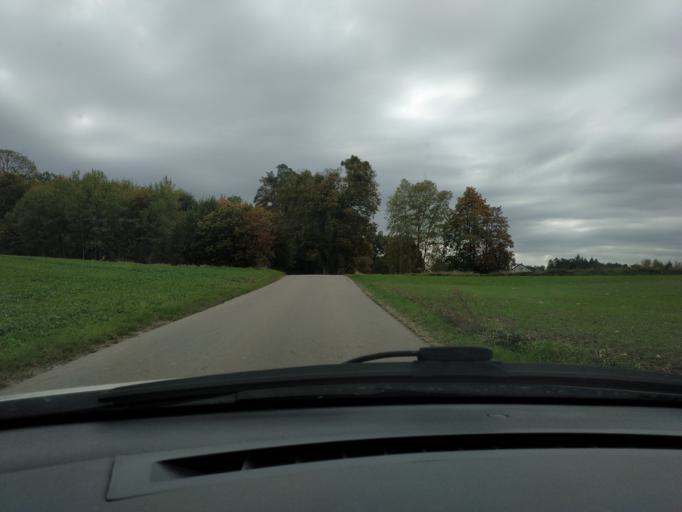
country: PL
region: Warmian-Masurian Voivodeship
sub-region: Powiat nowomiejski
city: Biskupiec
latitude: 53.4553
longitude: 19.3154
